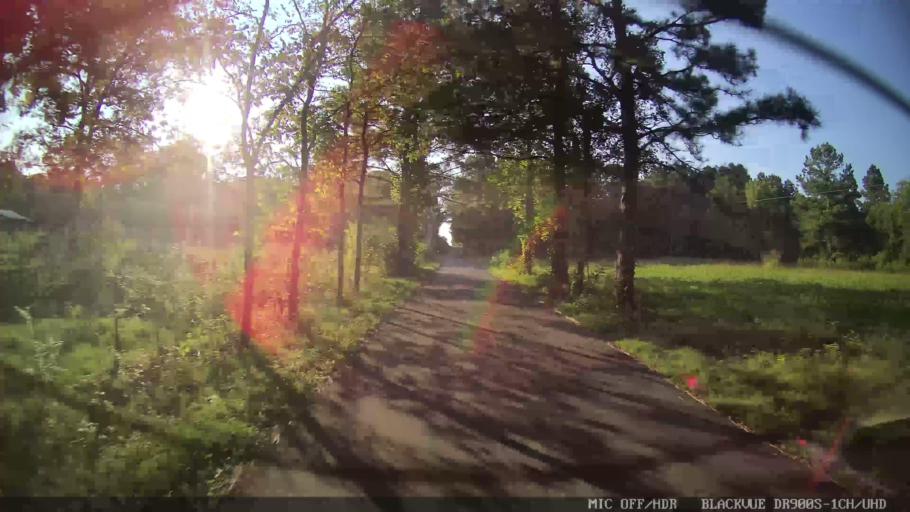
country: US
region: Tennessee
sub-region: Bradley County
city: Wildwood Lake
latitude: 35.0203
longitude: -84.7636
